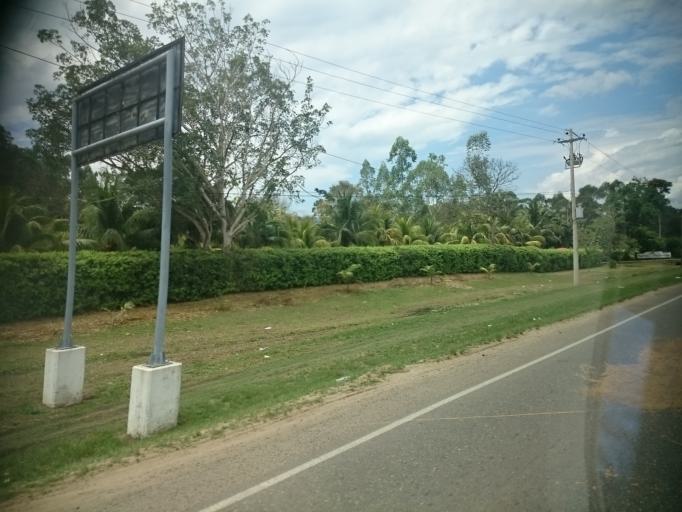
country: PE
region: San Martin
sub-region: Provincia de San Martin
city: Tarapoto
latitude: -6.5112
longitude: -76.3450
